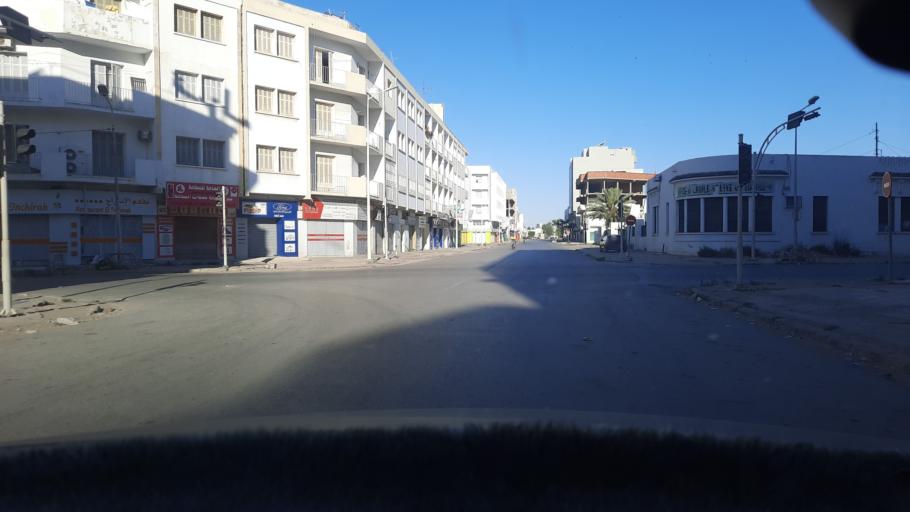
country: TN
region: Safaqis
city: Sfax
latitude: 34.7320
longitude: 10.7525
